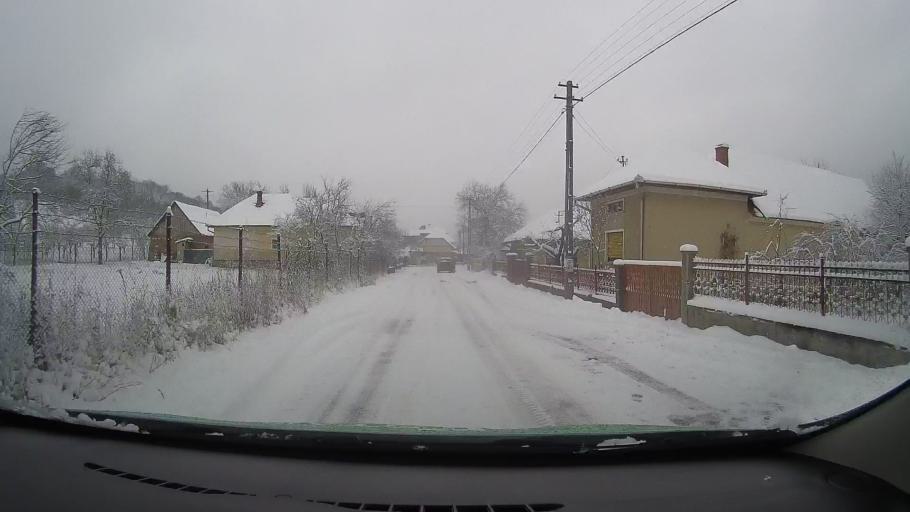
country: RO
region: Hunedoara
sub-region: Comuna Carjiti
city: Carjiti
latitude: 45.8290
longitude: 22.8469
